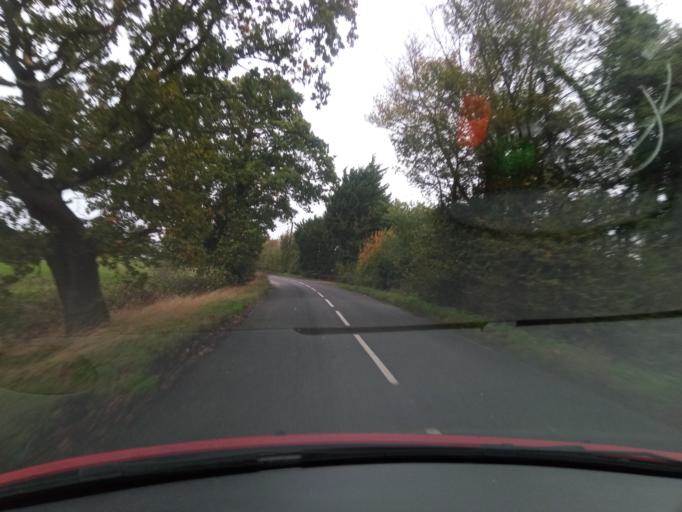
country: GB
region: England
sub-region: Essex
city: West Mersea
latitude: 51.7901
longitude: 0.9407
